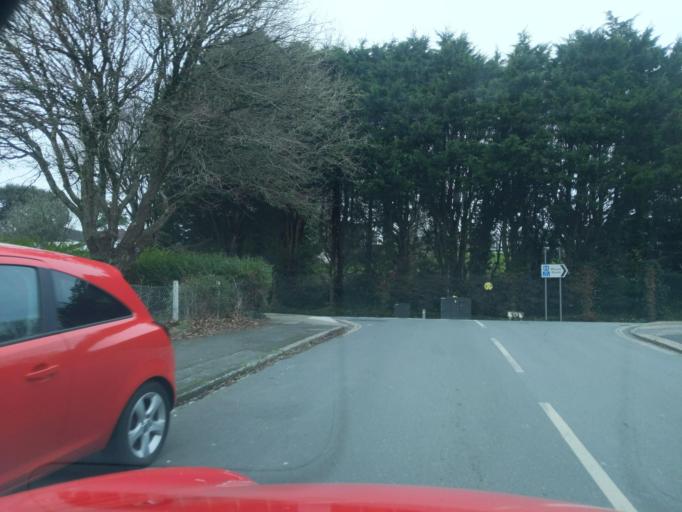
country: GB
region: England
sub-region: Plymouth
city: Plymstock
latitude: 50.3772
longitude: -4.1124
